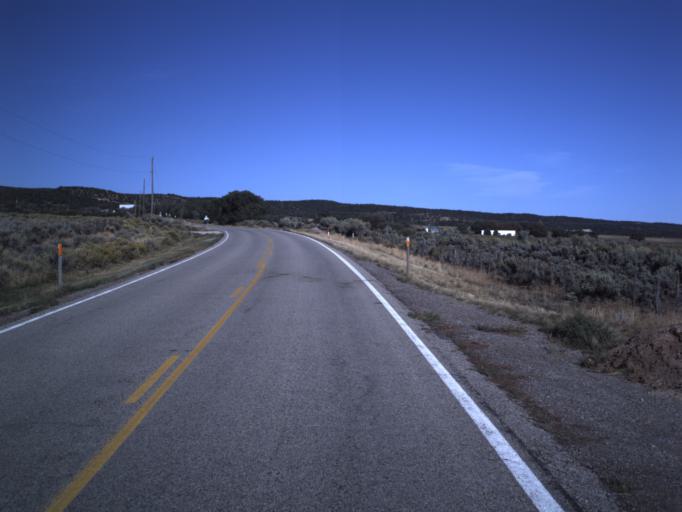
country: US
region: Utah
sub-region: Grand County
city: Moab
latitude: 38.3099
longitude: -109.2612
